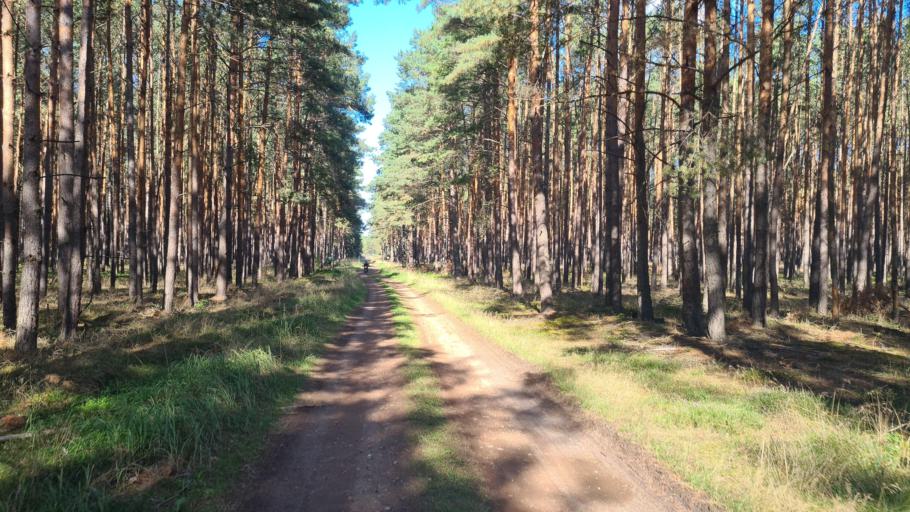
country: DE
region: Brandenburg
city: Hohenbucko
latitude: 51.8242
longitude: 13.5062
